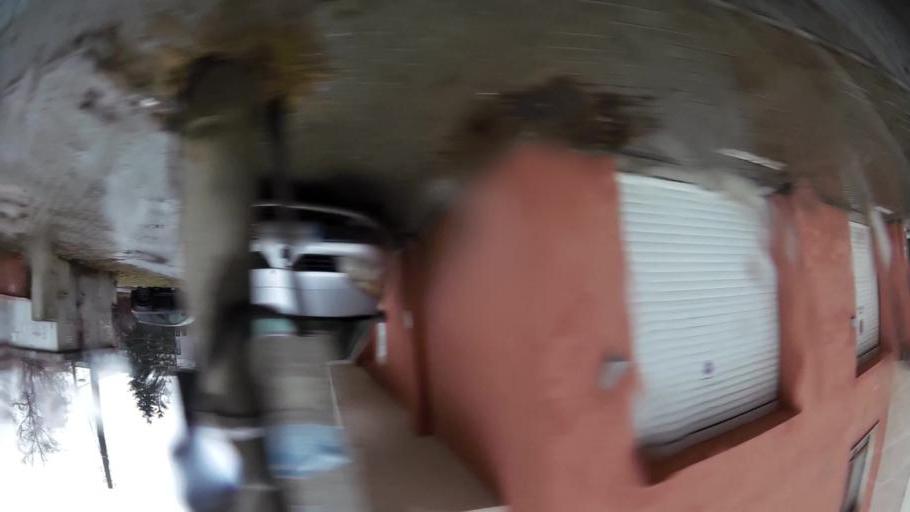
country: BG
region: Sofia-Capital
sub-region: Stolichna Obshtina
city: Sofia
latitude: 42.6482
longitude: 23.3323
